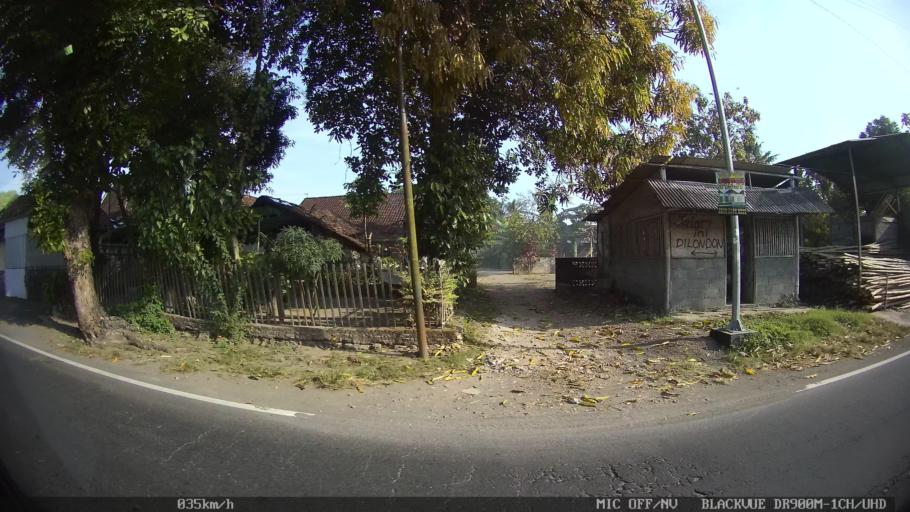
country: ID
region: Daerah Istimewa Yogyakarta
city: Bantul
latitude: -7.8779
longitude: 110.3257
